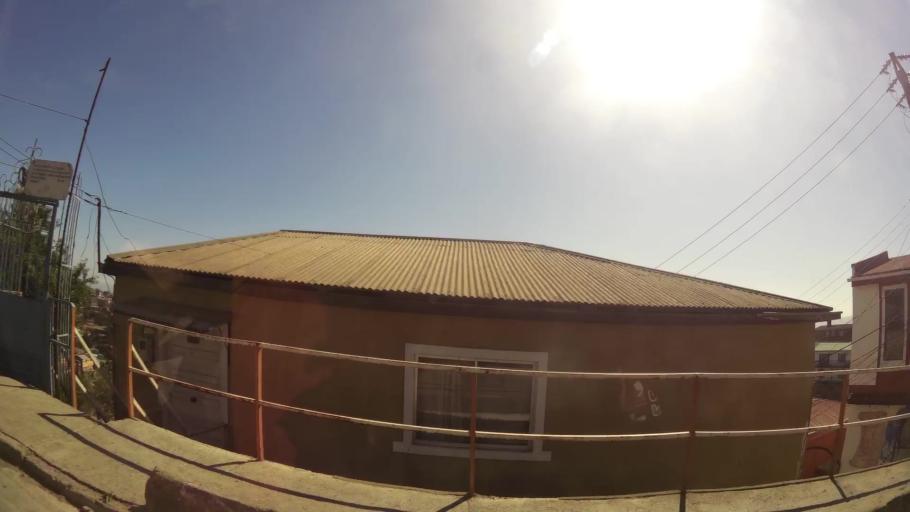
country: CL
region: Valparaiso
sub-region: Provincia de Valparaiso
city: Valparaiso
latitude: -33.0434
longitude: -71.6394
